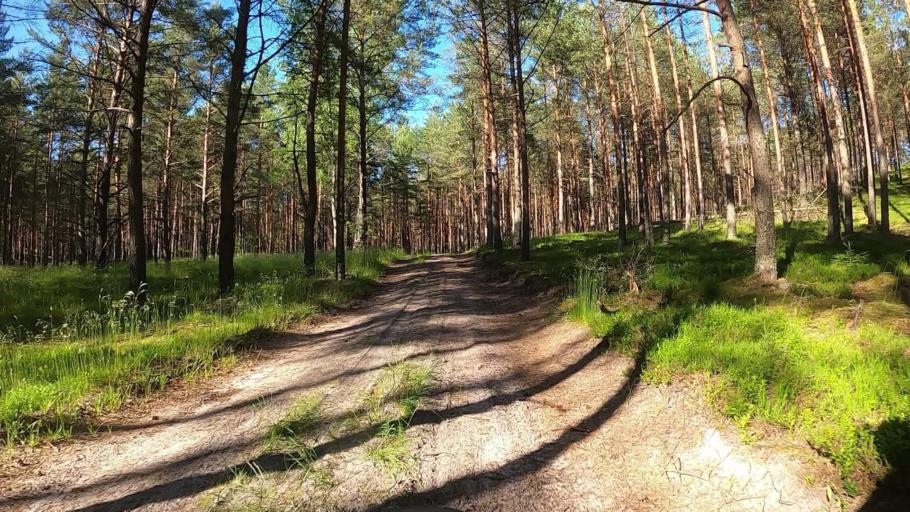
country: LV
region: Carnikava
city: Carnikava
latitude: 57.0889
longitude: 24.2547
